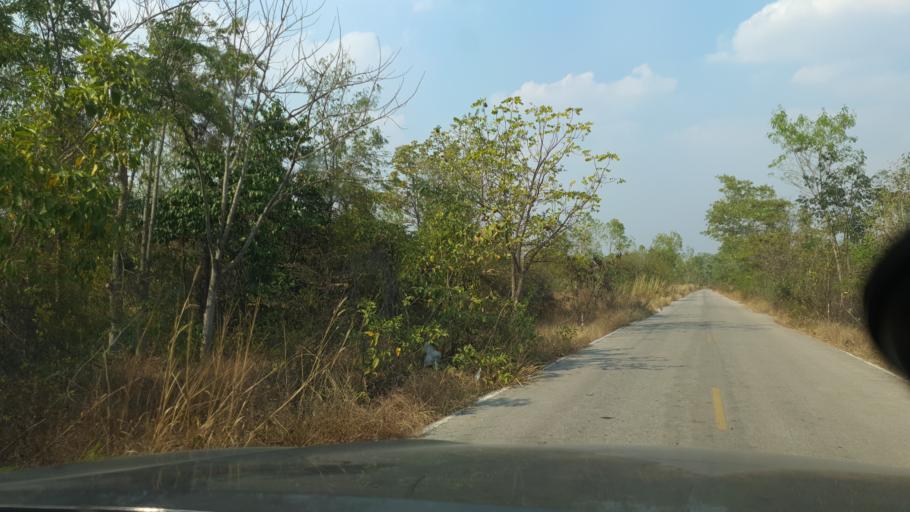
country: TH
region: Sukhothai
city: Ban Dan Lan Hoi
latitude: 17.0048
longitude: 99.5584
